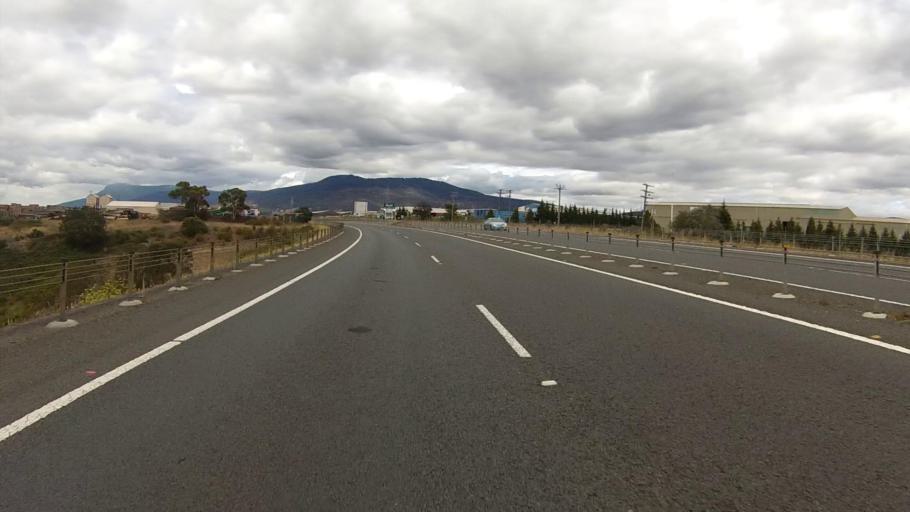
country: AU
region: Tasmania
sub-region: Brighton
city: Bridgewater
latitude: -42.7177
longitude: 147.2392
